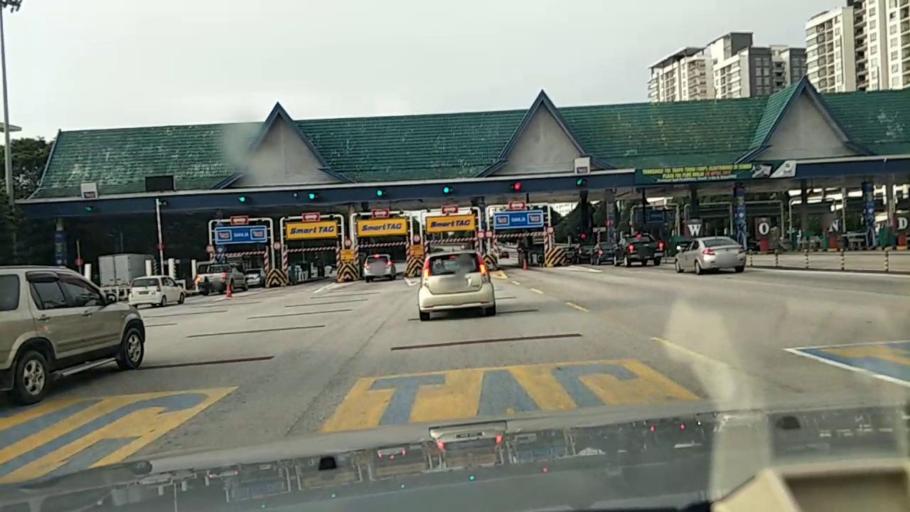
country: MY
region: Selangor
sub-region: Petaling
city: Petaling Jaya
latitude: 3.1024
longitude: 101.5903
